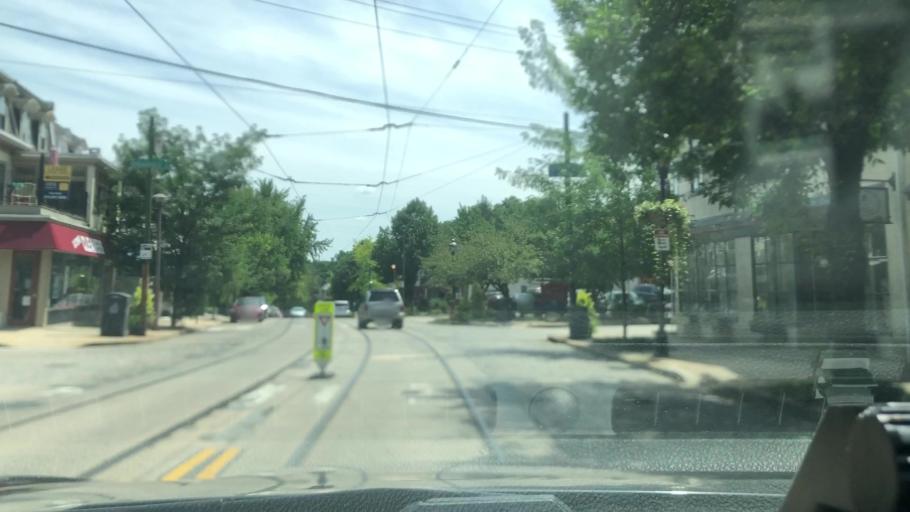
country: US
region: Pennsylvania
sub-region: Montgomery County
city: Wyndmoor
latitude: 40.0698
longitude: -75.2001
